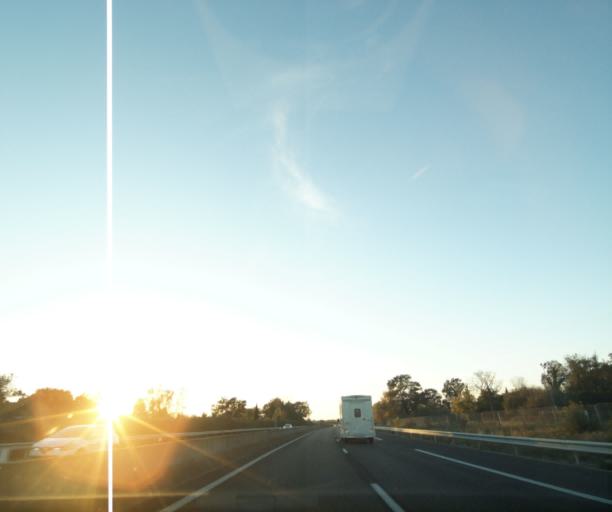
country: FR
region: Provence-Alpes-Cote d'Azur
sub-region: Departement des Bouches-du-Rhone
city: Salon-de-Provence
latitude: 43.6257
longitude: 5.0955
